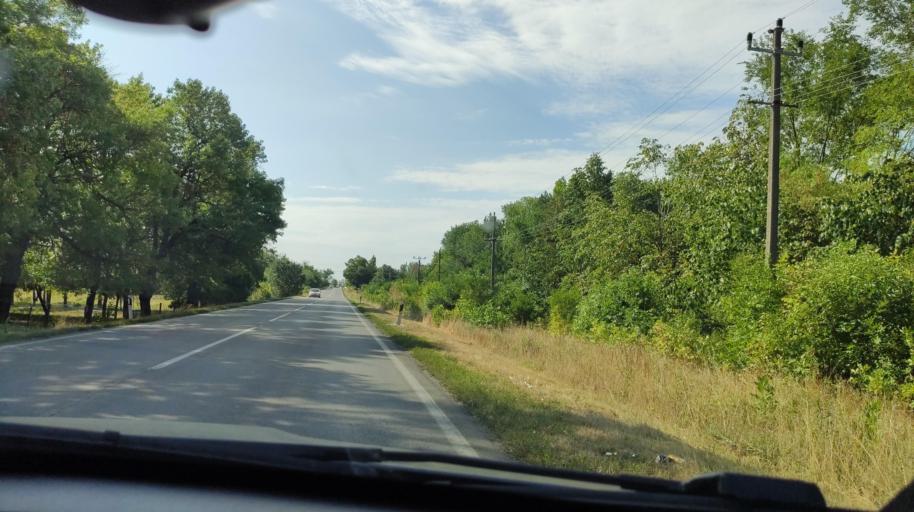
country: RS
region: Autonomna Pokrajina Vojvodina
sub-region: Severnobacki Okrug
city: Backa Topola
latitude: 45.8042
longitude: 19.6320
